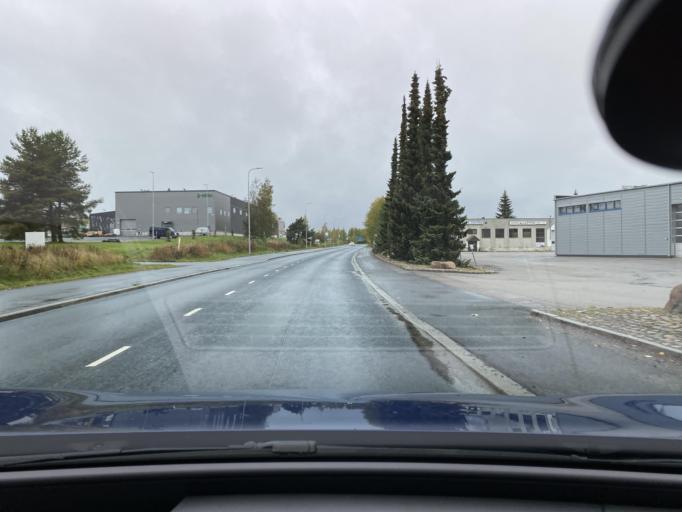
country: FI
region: Pirkanmaa
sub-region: Tampere
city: Tampere
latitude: 61.4579
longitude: 23.7318
